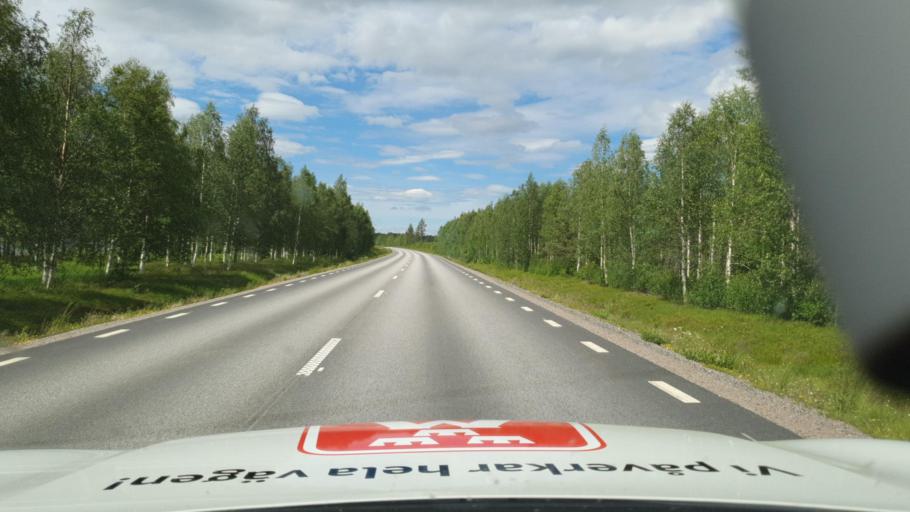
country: SE
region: Vaesterbotten
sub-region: Norsjo Kommun
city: Norsjoe
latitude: 65.1941
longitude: 19.8353
